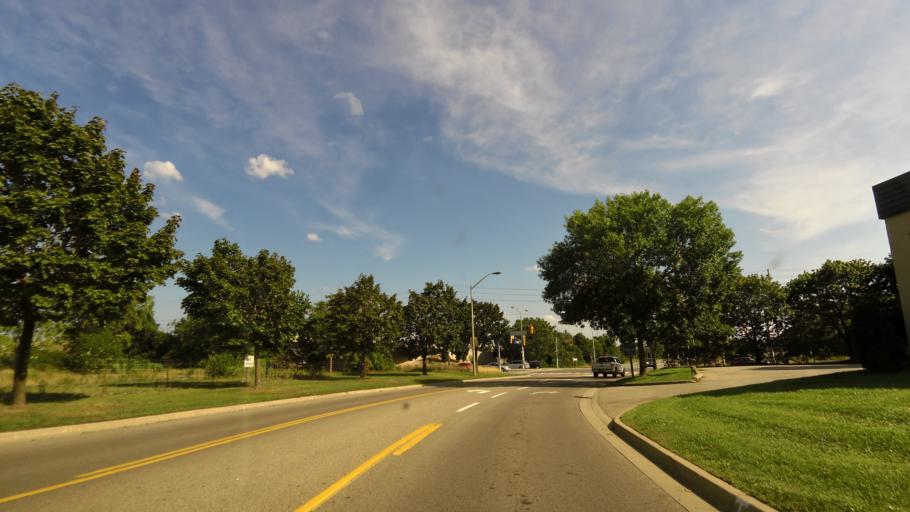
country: CA
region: Ontario
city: Burlington
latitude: 43.3288
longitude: -79.8243
